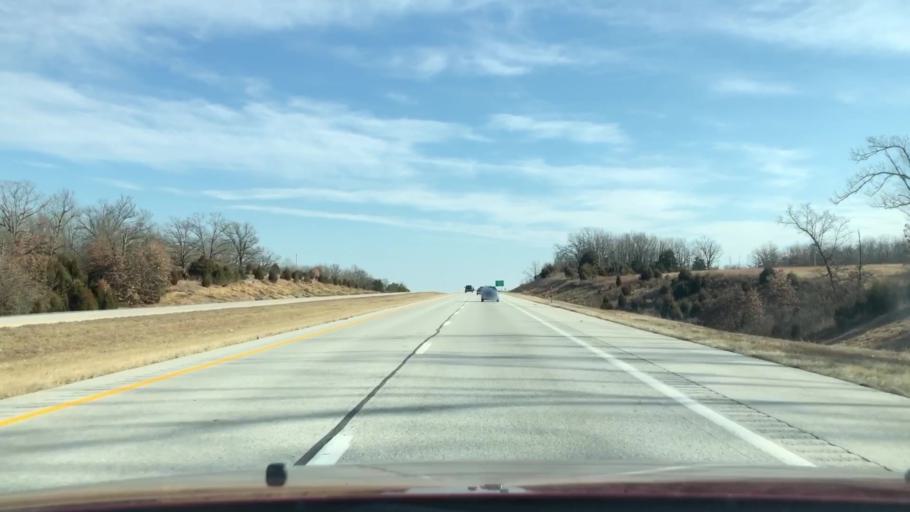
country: US
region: Missouri
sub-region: Webster County
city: Seymour
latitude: 37.1617
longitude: -92.8903
